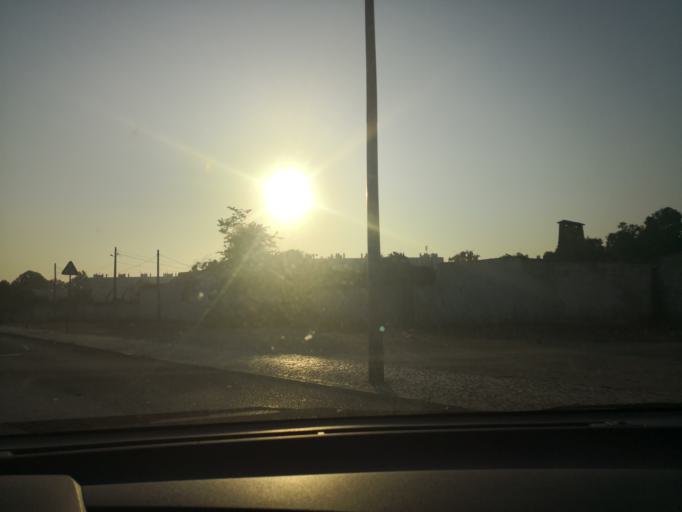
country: PT
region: Setubal
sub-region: Moita
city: Alhos Vedros
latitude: 38.6496
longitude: -9.0399
